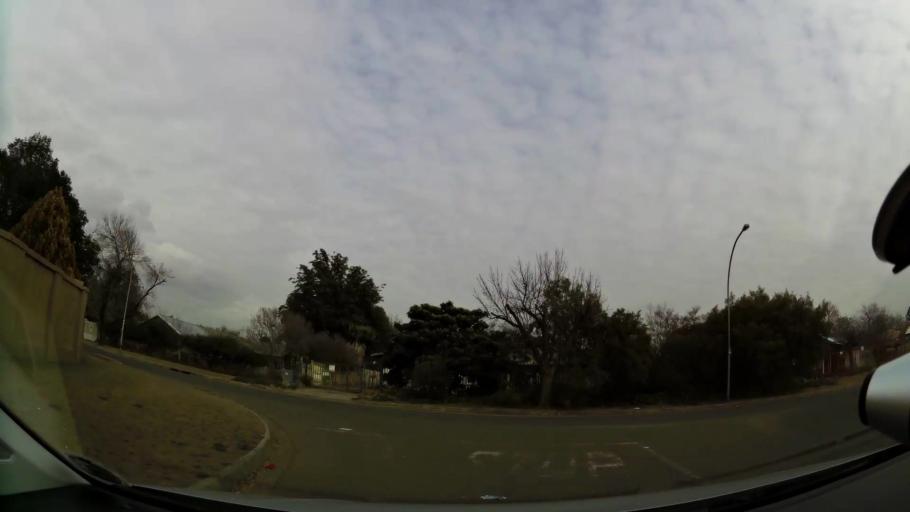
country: ZA
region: Orange Free State
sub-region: Mangaung Metropolitan Municipality
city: Bloemfontein
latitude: -29.1241
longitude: 26.1889
